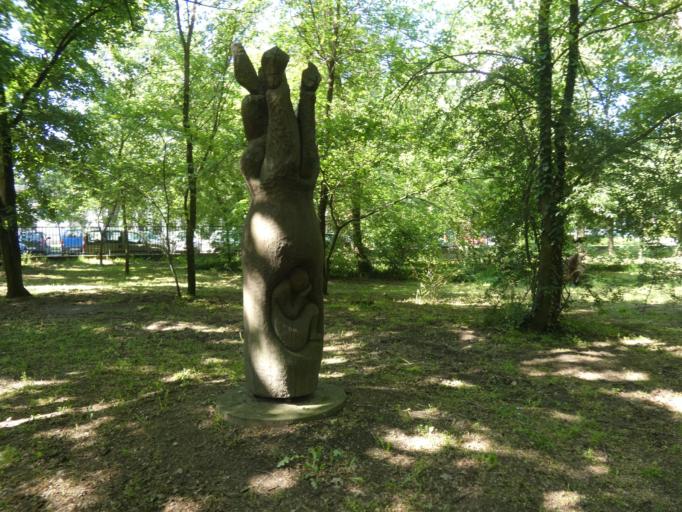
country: HU
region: Hajdu-Bihar
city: Debrecen
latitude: 47.5509
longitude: 21.6319
